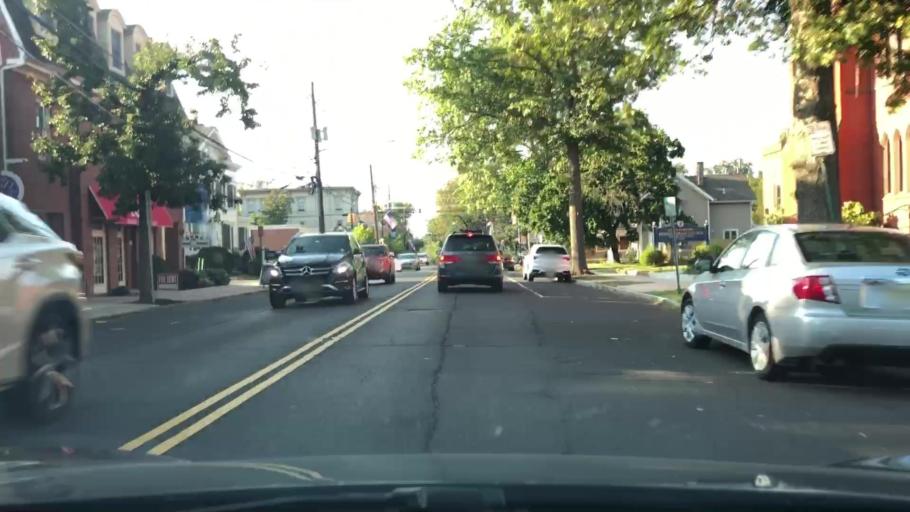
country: US
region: New Jersey
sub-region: Mercer County
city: Pennington
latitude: 40.3272
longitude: -74.7908
